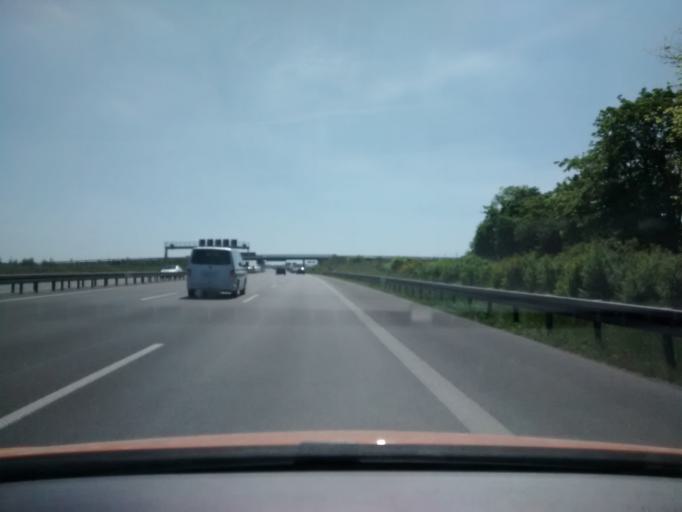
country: DE
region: Brandenburg
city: Schonefeld
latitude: 52.3875
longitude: 13.5294
